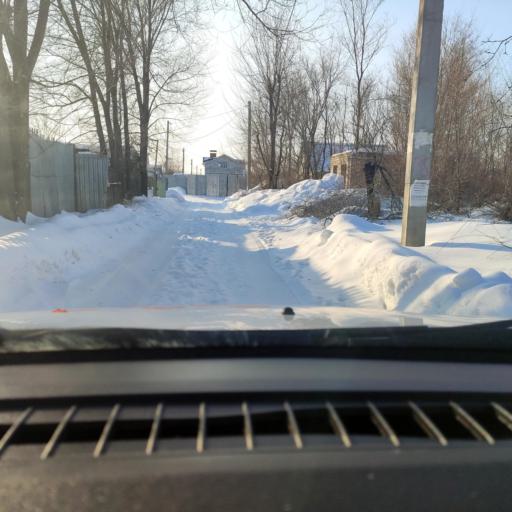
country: RU
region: Samara
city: Samara
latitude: 53.1297
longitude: 50.2551
